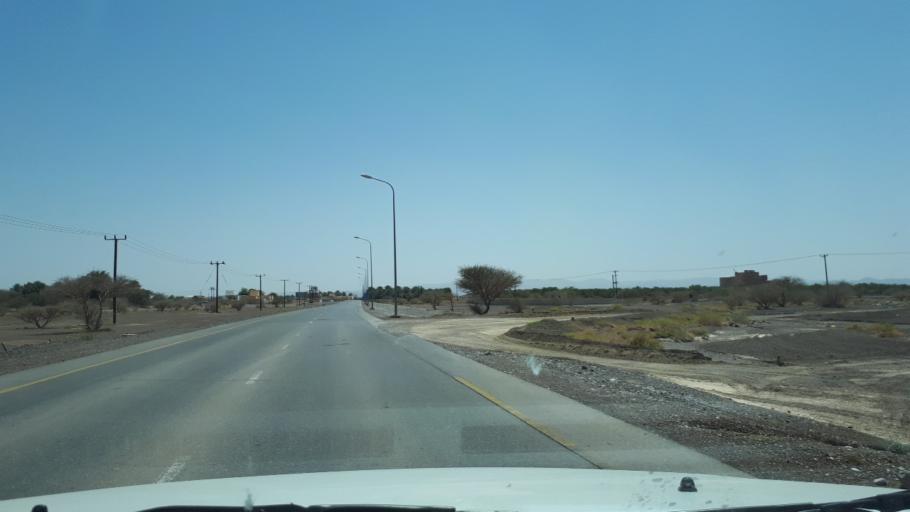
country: OM
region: Muhafazat ad Dakhiliyah
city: Bahla'
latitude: 22.9196
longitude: 57.2545
